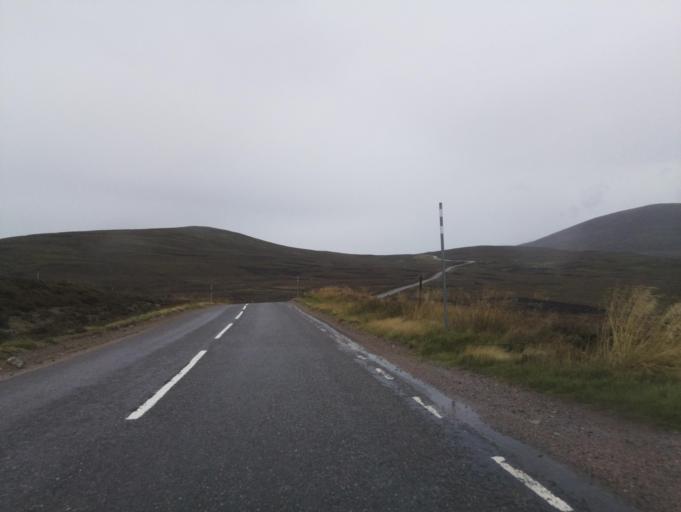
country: GB
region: Scotland
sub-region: Aberdeenshire
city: Ballater
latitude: 57.1510
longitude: -3.1664
